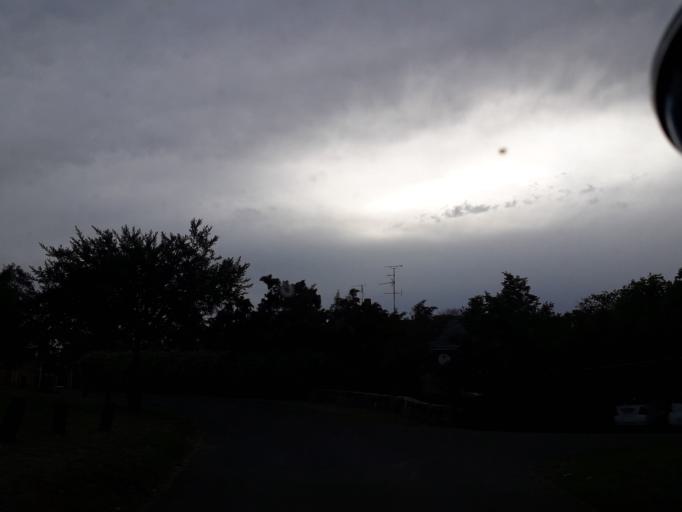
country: ZA
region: Gauteng
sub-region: City of Johannesburg Metropolitan Municipality
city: Johannesburg
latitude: -26.0879
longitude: 28.0146
